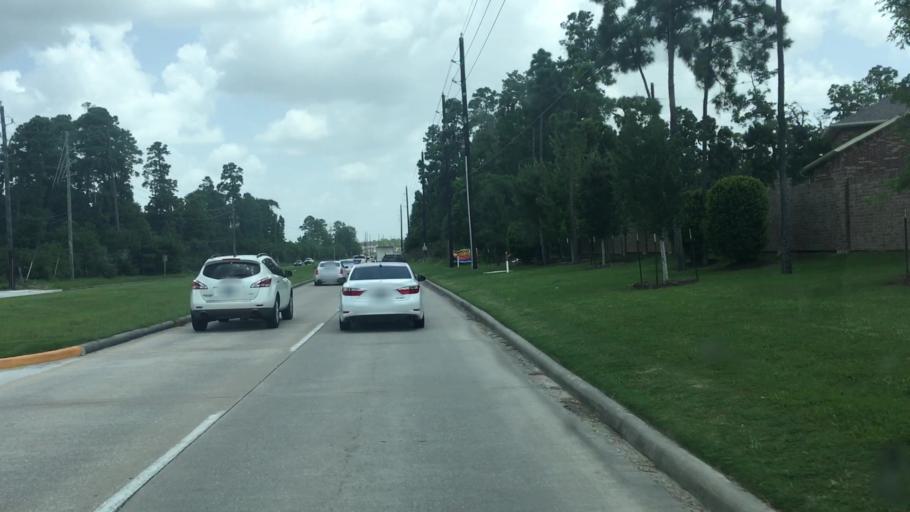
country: US
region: Texas
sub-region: Harris County
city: Atascocita
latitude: 29.9396
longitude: -95.1755
